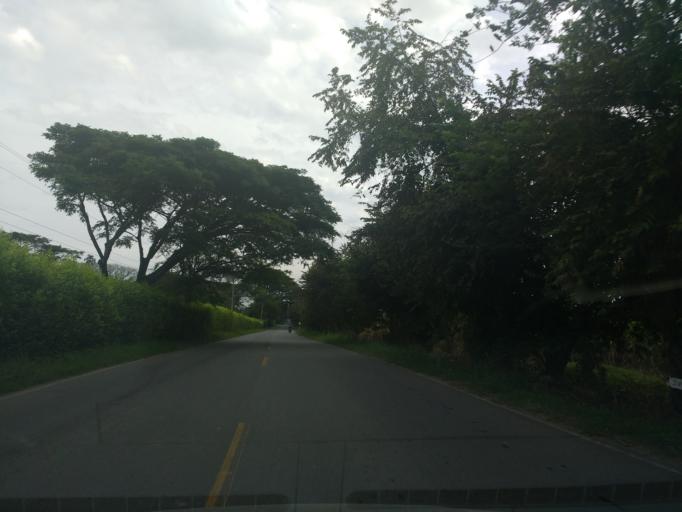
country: CO
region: Valle del Cauca
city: Florida
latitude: 3.3043
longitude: -76.2330
